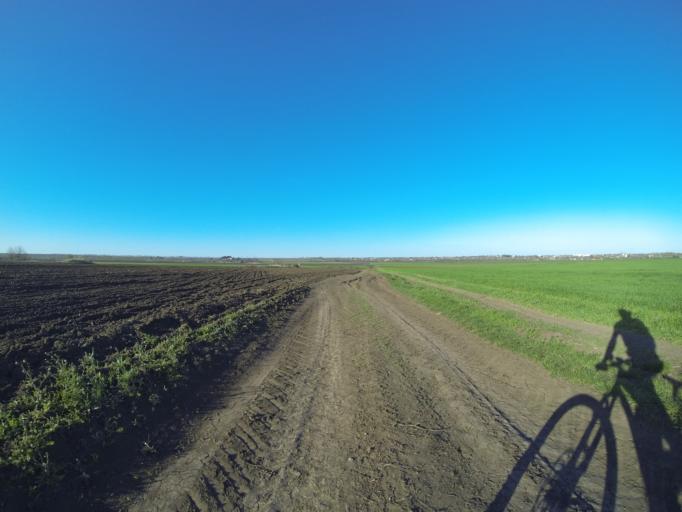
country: RO
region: Dolj
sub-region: Comuna Segarcea
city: Segarcea
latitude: 44.0892
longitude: 23.7159
